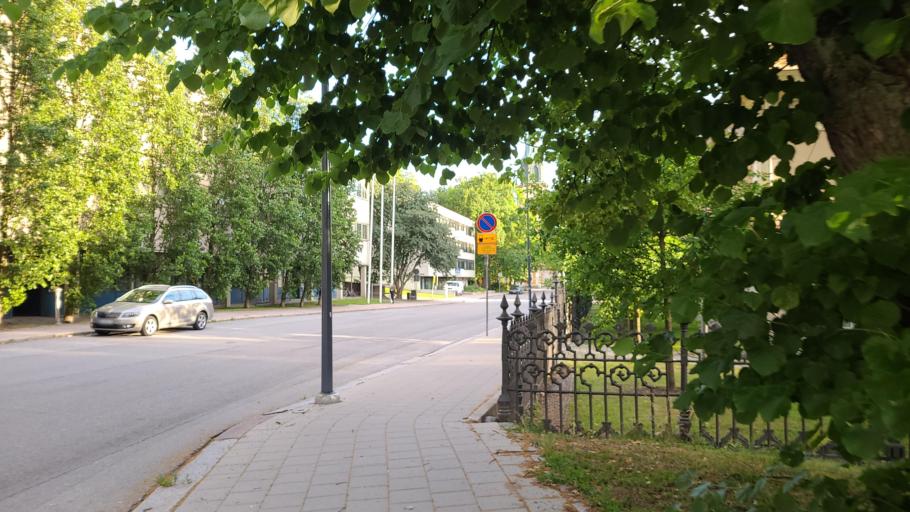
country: FI
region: Varsinais-Suomi
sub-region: Turku
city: Turku
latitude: 60.4558
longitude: 22.2801
